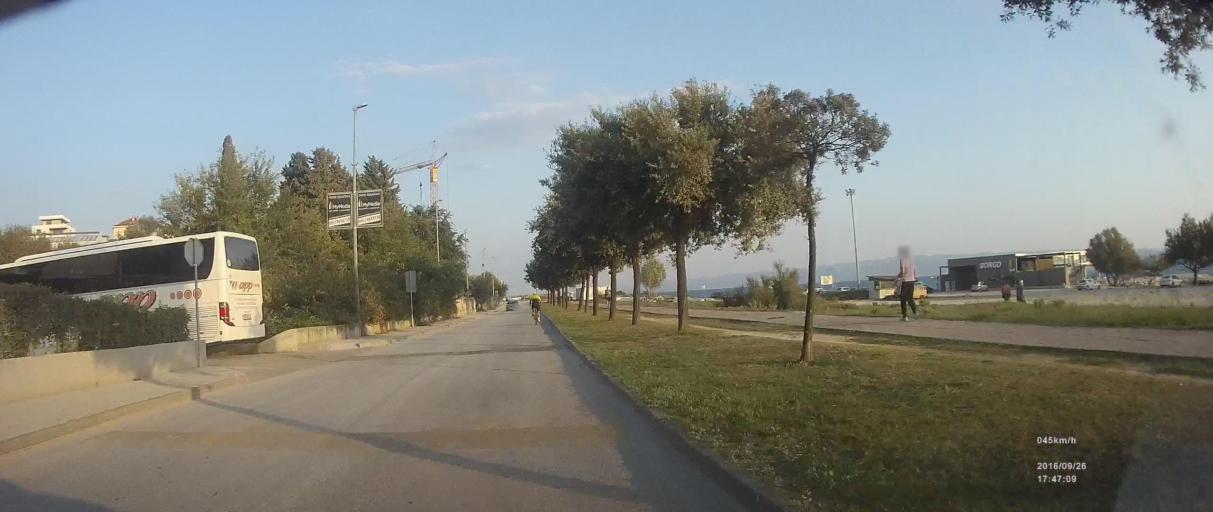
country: HR
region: Splitsko-Dalmatinska
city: Vranjic
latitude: 43.5030
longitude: 16.4800
